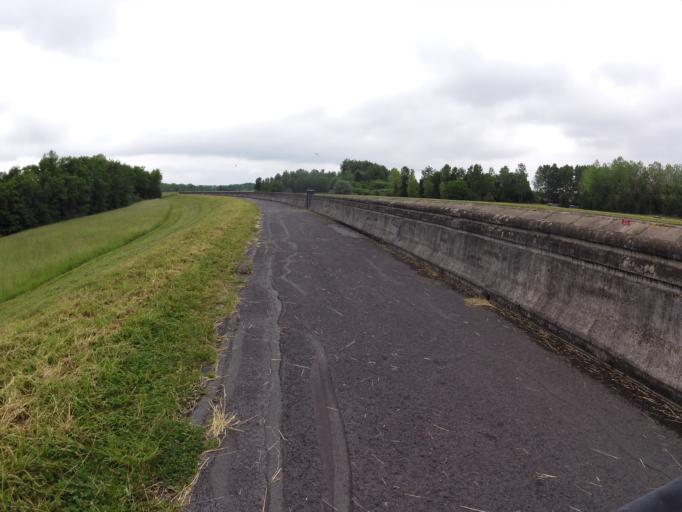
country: FR
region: Champagne-Ardenne
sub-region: Departement de la Haute-Marne
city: Villiers-en-Lieu
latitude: 48.5994
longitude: 4.8624
